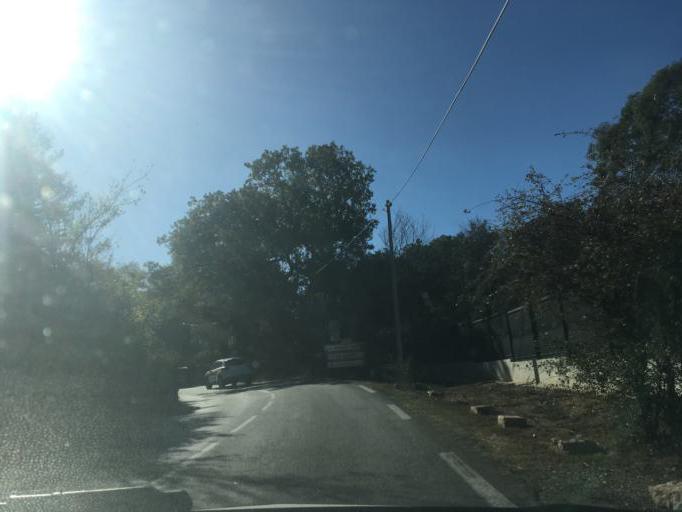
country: FR
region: Provence-Alpes-Cote d'Azur
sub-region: Departement du Var
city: La Garde-Freinet
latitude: 43.3177
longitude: 6.4723
